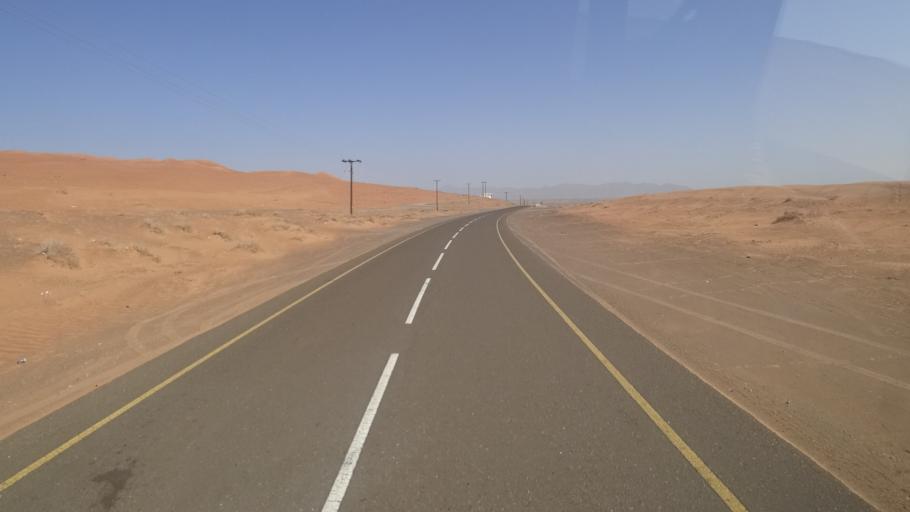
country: OM
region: Ash Sharqiyah
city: Al Qabil
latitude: 22.4943
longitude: 58.7153
